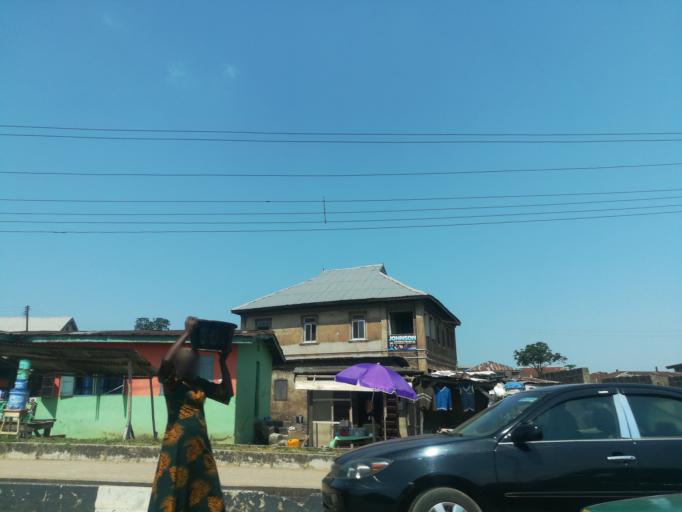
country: NG
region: Ogun
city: Abeokuta
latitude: 7.1497
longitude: 3.3562
